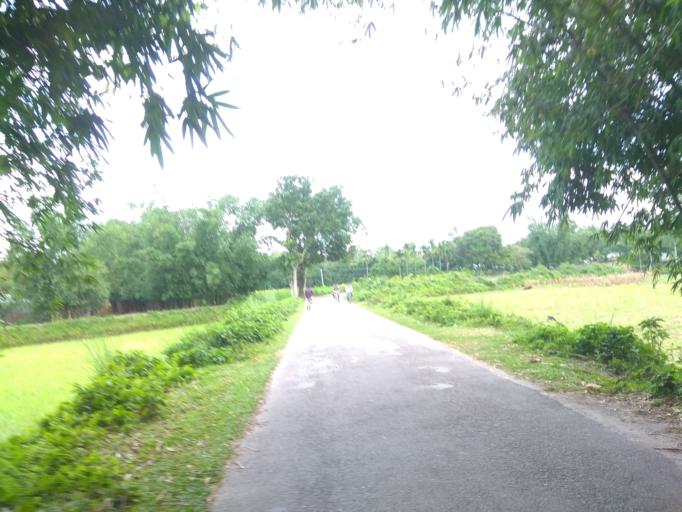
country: IN
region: West Bengal
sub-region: Koch Bihar
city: Haldibari
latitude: 26.2028
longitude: 88.9206
